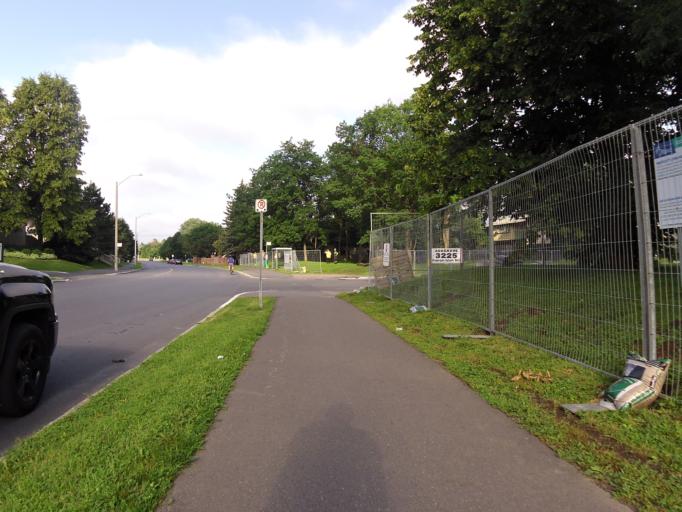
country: CA
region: Ontario
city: Ottawa
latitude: 45.3496
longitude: -75.6768
